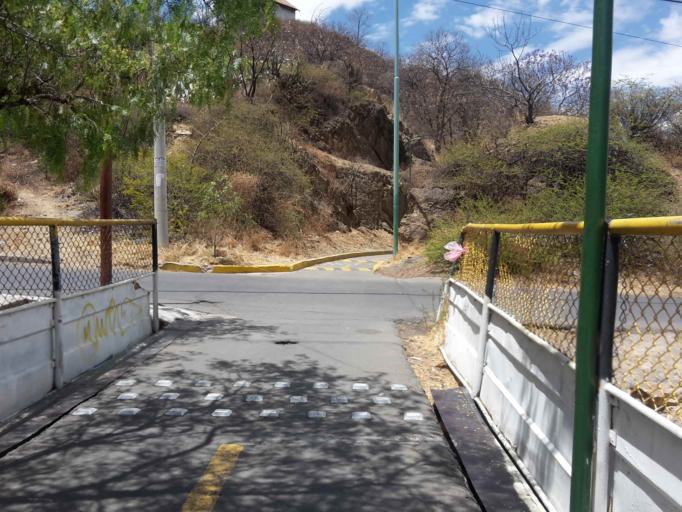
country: BO
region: Cochabamba
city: Cochabamba
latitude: -17.3771
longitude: -66.1380
